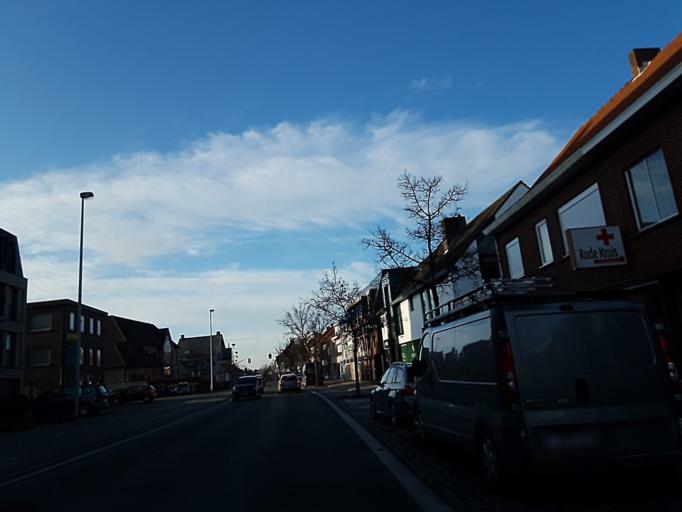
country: BE
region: Flanders
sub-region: Provincie Antwerpen
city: Oud-Turnhout
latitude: 51.3171
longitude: 4.9843
